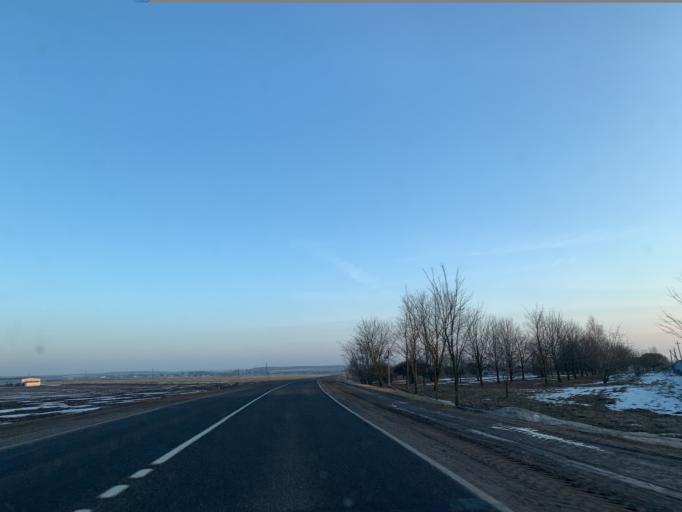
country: BY
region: Minsk
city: Haradzyeya
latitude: 53.3194
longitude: 26.5589
